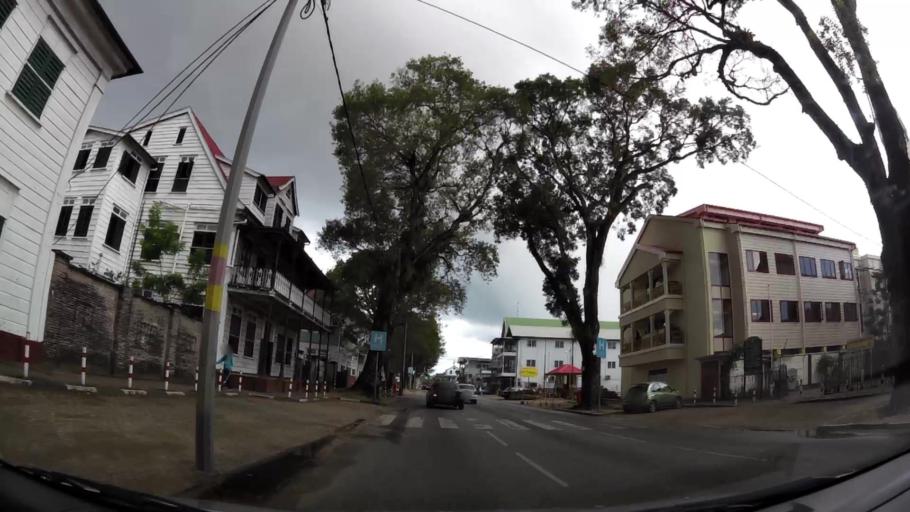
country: SR
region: Paramaribo
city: Paramaribo
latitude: 5.8302
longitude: -55.1576
